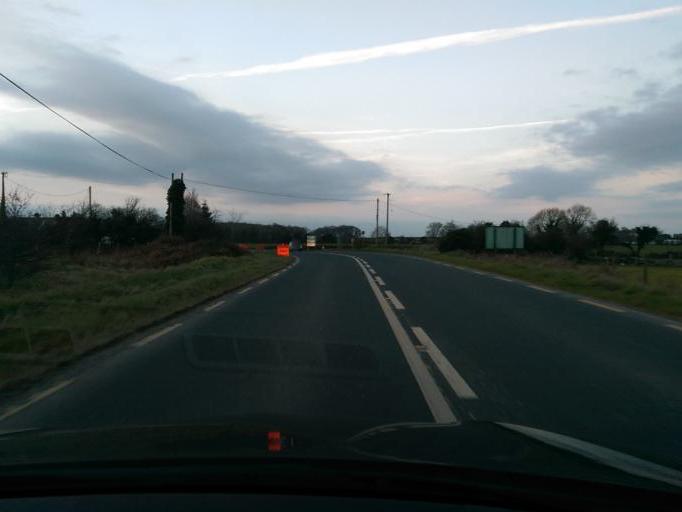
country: IE
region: Connaught
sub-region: County Galway
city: Portumna
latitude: 53.0198
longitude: -8.1256
